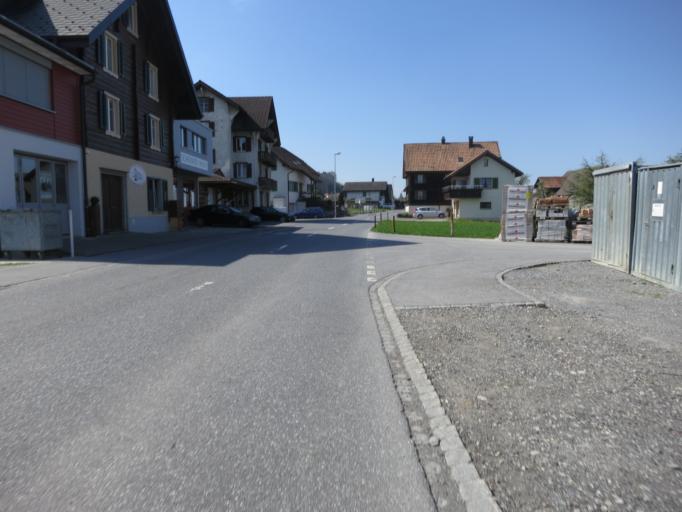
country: CH
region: Schwyz
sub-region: Bezirk March
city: Lachen
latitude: 47.1737
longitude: 8.8883
